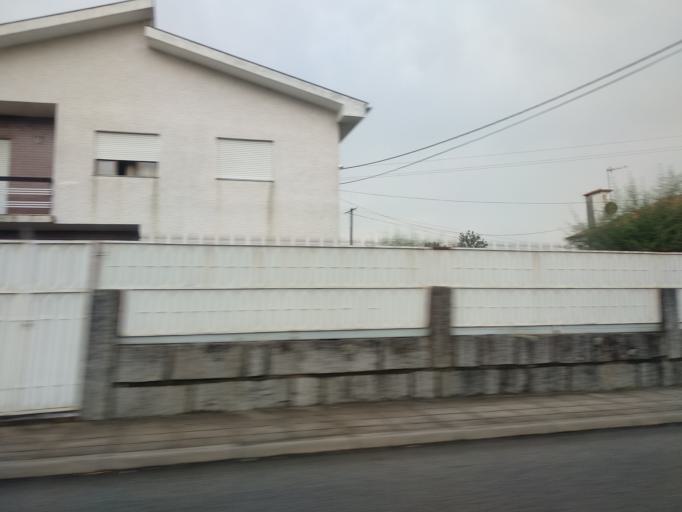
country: PT
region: Braga
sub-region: Vila Nova de Famalicao
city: Vila Nova de Famalicao
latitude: 41.4043
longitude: -8.5022
